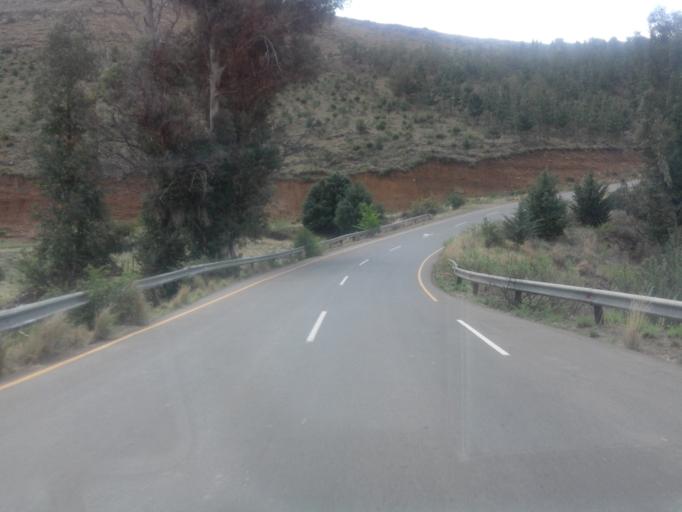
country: LS
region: Qacha's Nek
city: Qacha's Nek
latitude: -30.0782
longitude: 28.6207
